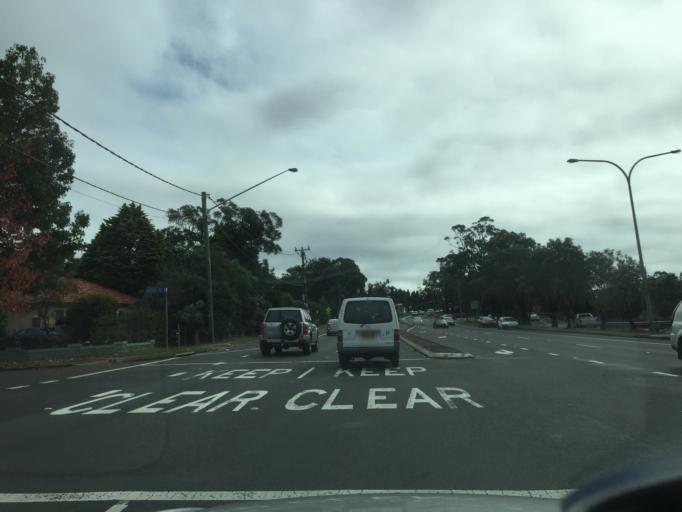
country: AU
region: New South Wales
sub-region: Blue Mountains Municipality
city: Blaxland
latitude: -33.7394
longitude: 150.6053
